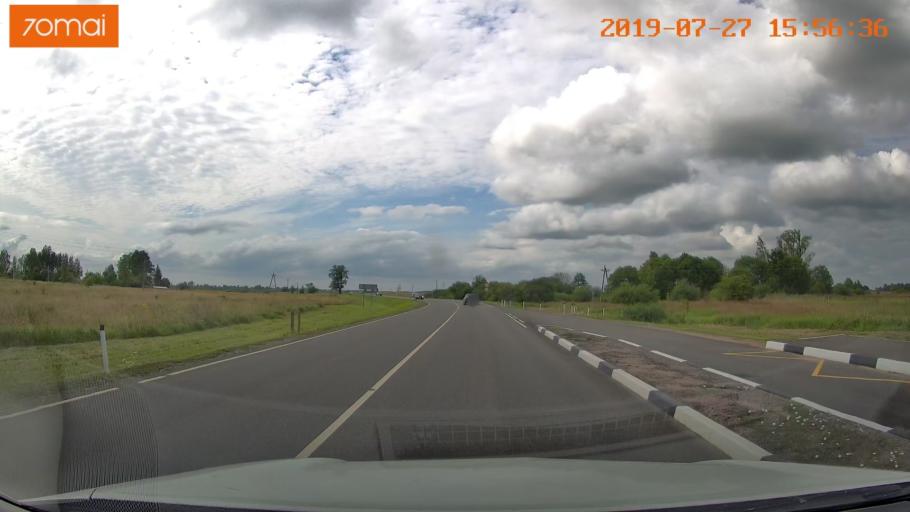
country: RU
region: Kaliningrad
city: Chernyakhovsk
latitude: 54.6202
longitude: 21.8992
